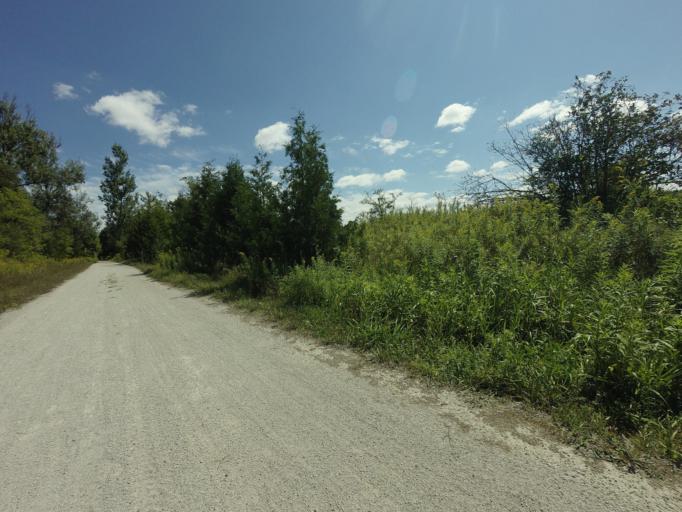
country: CA
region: Ontario
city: Orangeville
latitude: 43.7755
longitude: -80.1047
